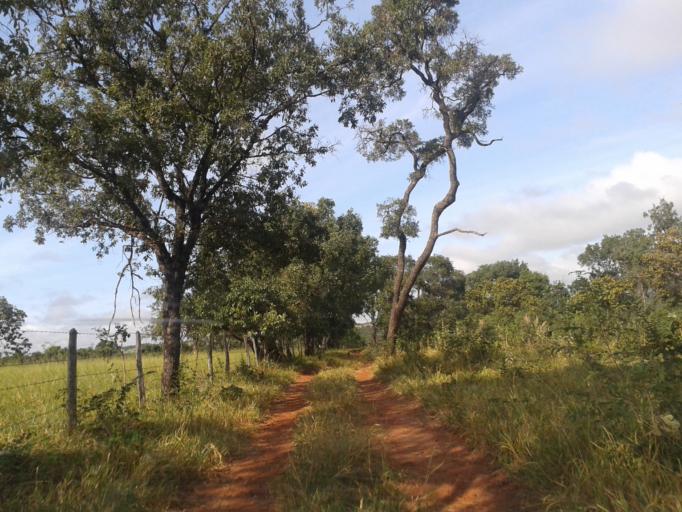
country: BR
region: Minas Gerais
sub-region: Campina Verde
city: Campina Verde
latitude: -19.4242
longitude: -49.6552
